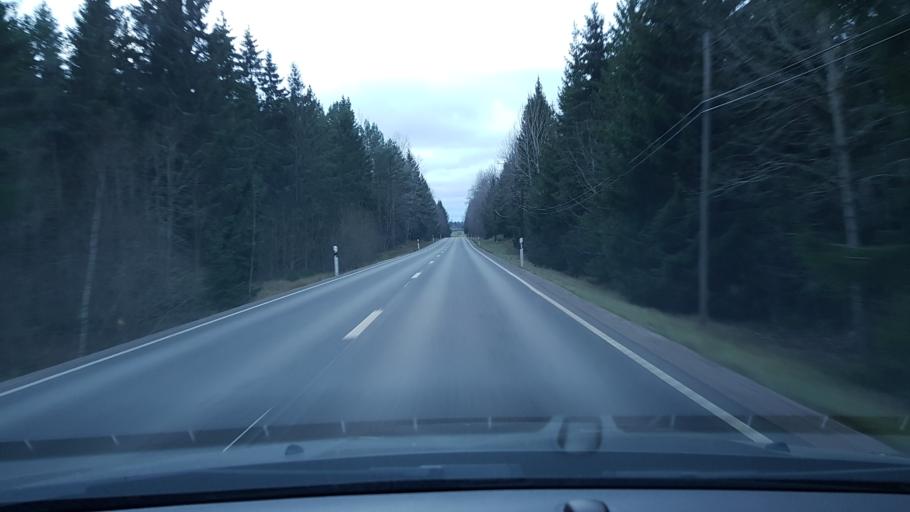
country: SE
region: Uppsala
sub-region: Uppsala Kommun
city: Vattholma
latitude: 59.9484
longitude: 17.9439
